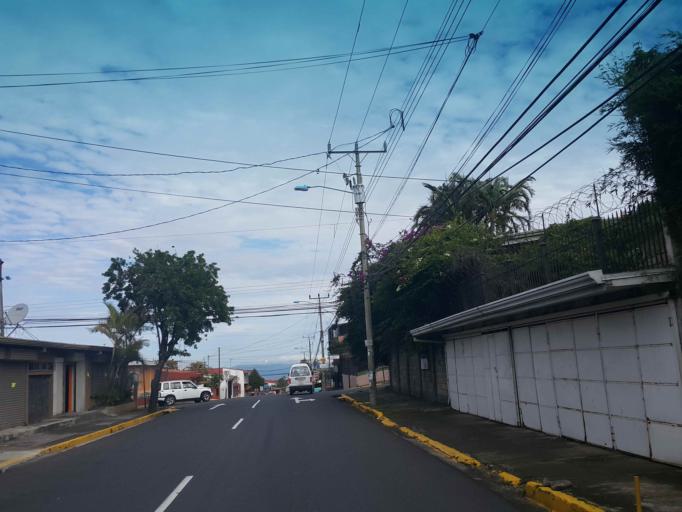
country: CR
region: Heredia
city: Heredia
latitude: 10.0046
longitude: -84.1155
